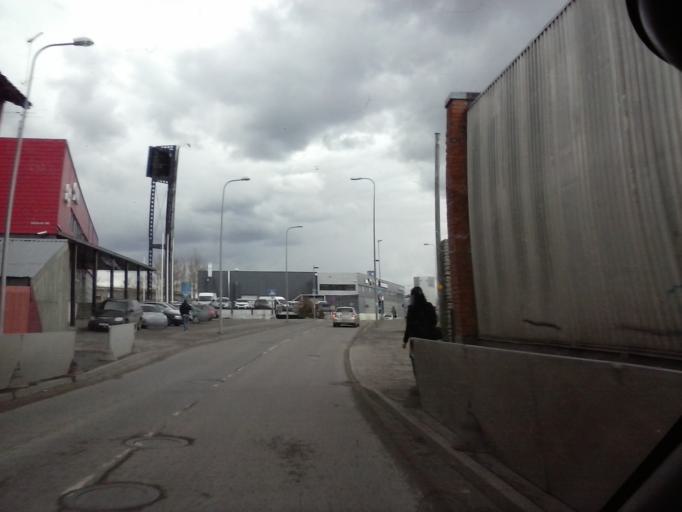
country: EE
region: Harju
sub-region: Tallinna linn
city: Tallinn
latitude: 59.4262
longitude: 24.7869
